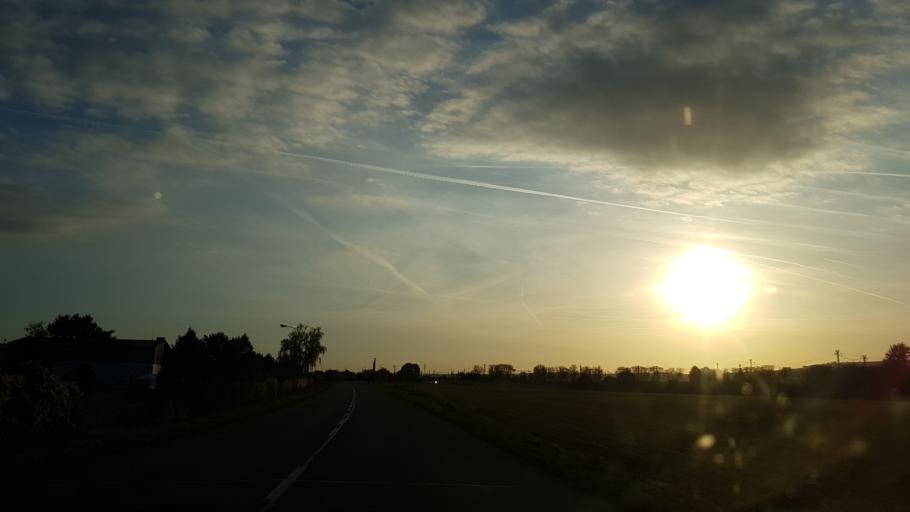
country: CZ
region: Zlin
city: Nedakonice
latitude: 49.0405
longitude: 17.3880
